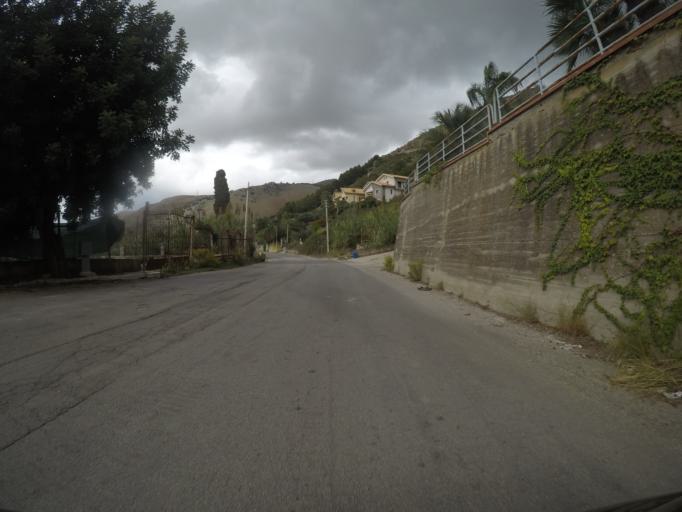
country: IT
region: Sicily
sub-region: Palermo
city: Montelepre
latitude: 38.0931
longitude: 13.1703
